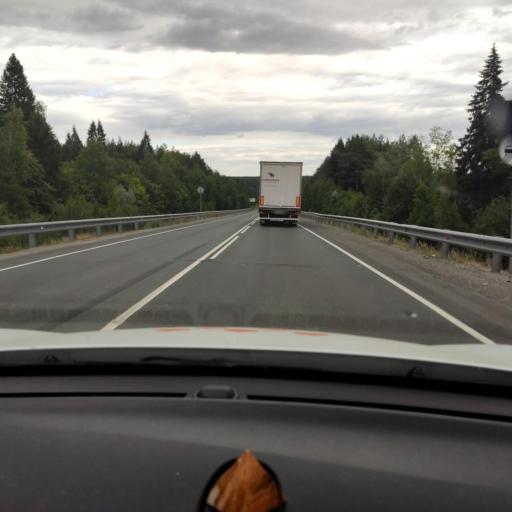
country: RU
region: Mariy-El
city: Volzhsk
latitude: 55.9069
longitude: 48.3761
